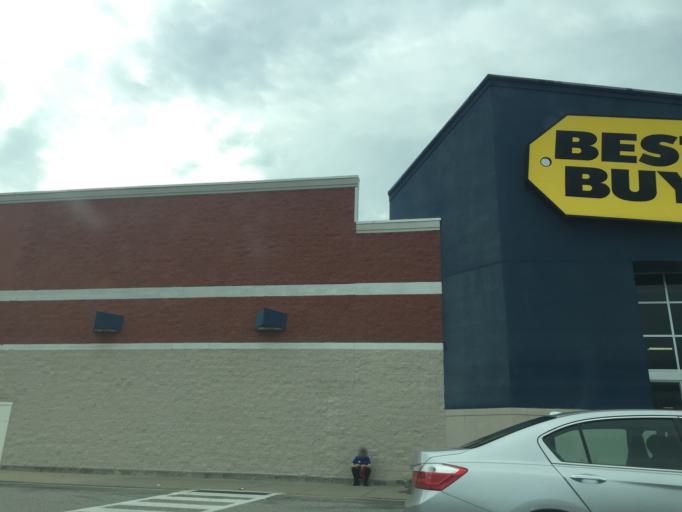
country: US
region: Virginia
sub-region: York County
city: Yorktown
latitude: 37.1081
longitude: -76.4982
